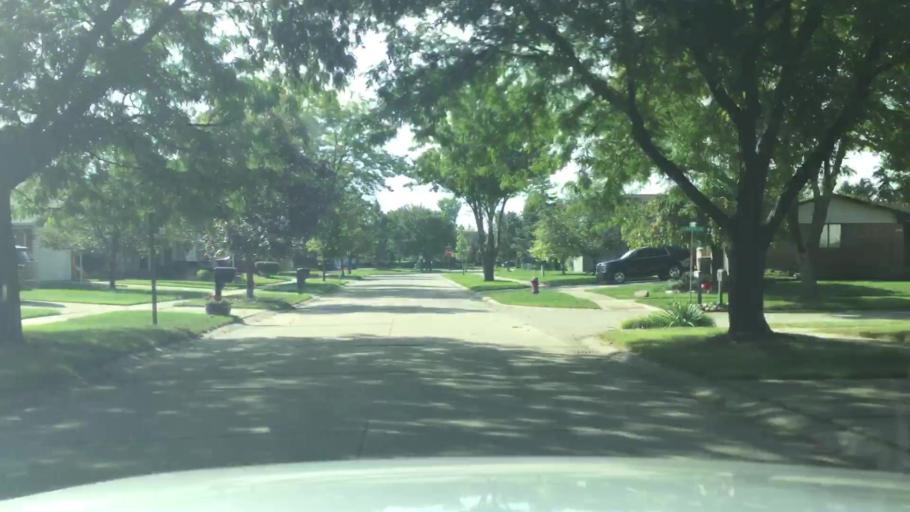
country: US
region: Michigan
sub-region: Wayne County
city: Canton
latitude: 42.3307
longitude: -83.4914
